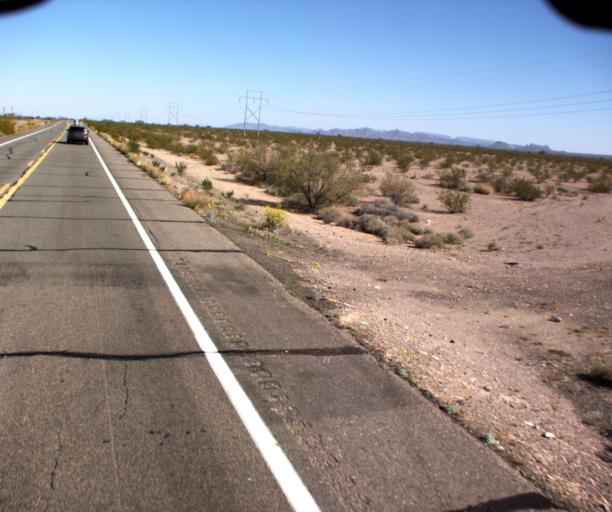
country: US
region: Arizona
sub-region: La Paz County
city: Quartzsite
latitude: 33.3342
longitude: -114.2170
